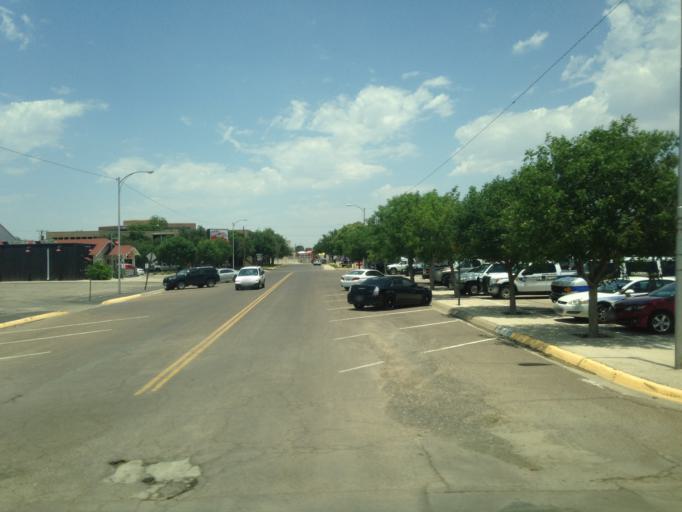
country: US
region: Texas
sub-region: Midland County
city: Midland
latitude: 32.0026
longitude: -102.0771
